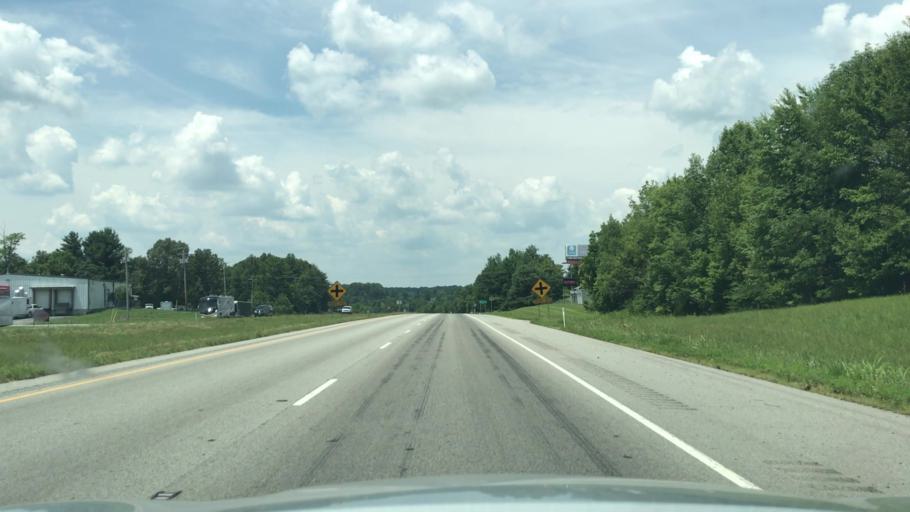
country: US
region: Tennessee
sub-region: Putnam County
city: Algood
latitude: 36.2073
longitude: -85.4407
